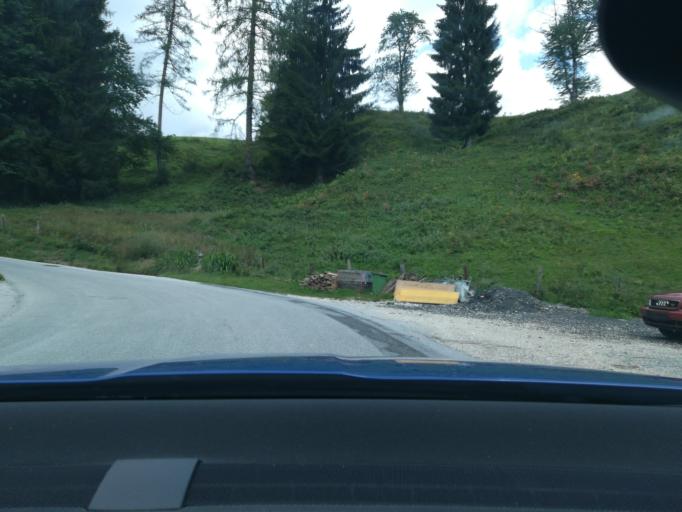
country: AT
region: Salzburg
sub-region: Politischer Bezirk Hallein
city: Abtenau
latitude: 47.5760
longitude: 13.3906
